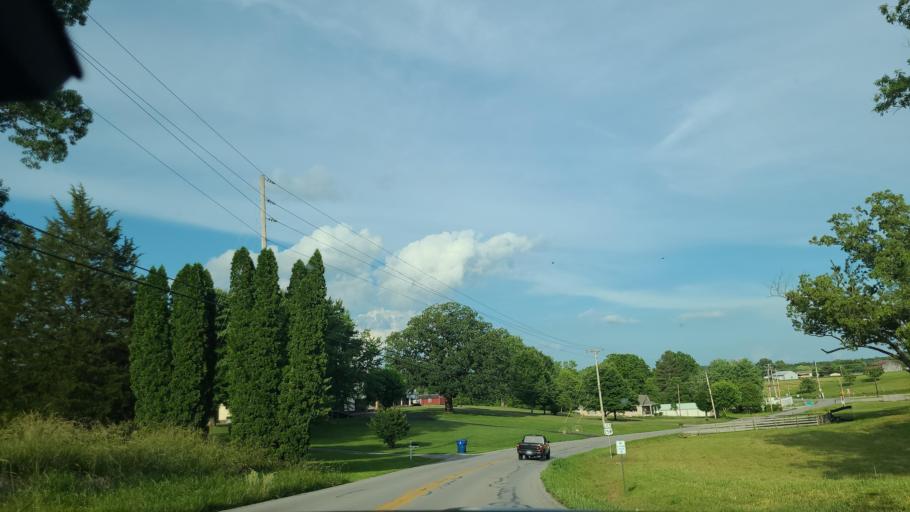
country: US
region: Kentucky
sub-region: Whitley County
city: Corbin
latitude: 36.8823
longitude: -84.2030
